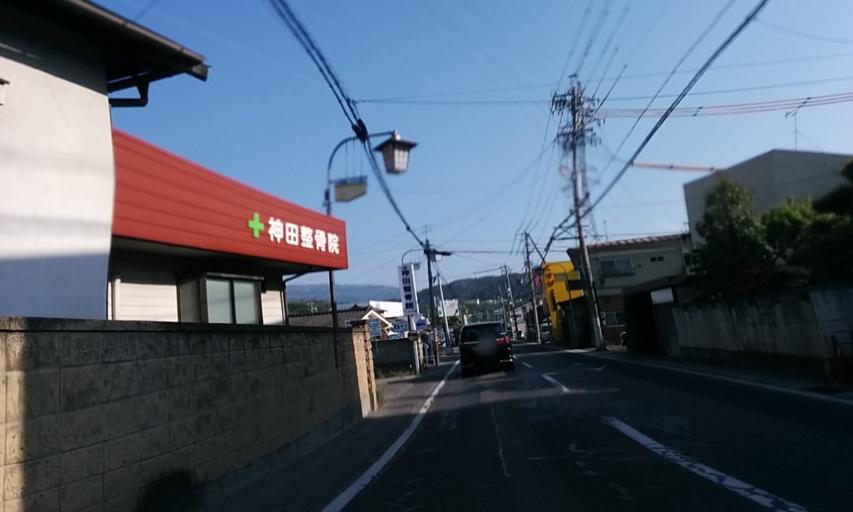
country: JP
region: Nagano
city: Matsumoto
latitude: 36.2233
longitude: 137.9858
